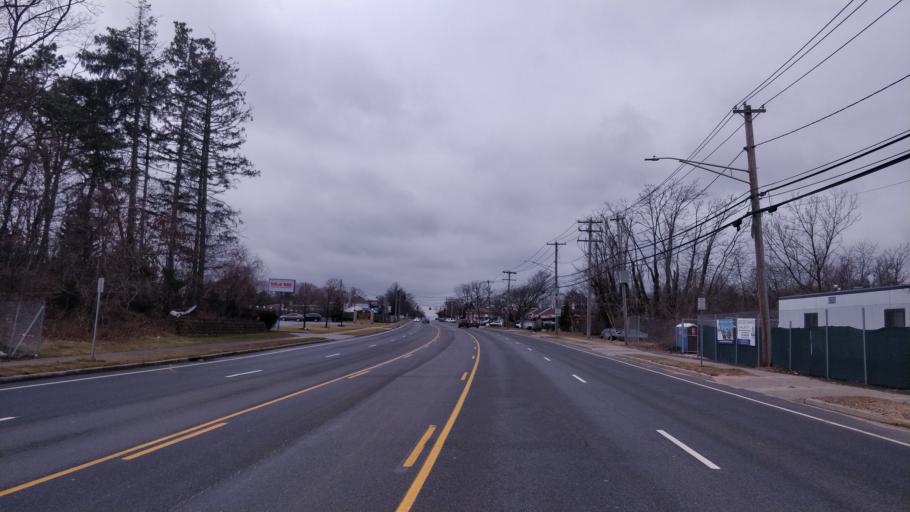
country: US
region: New York
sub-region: Suffolk County
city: Commack
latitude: 40.8469
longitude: -73.2629
